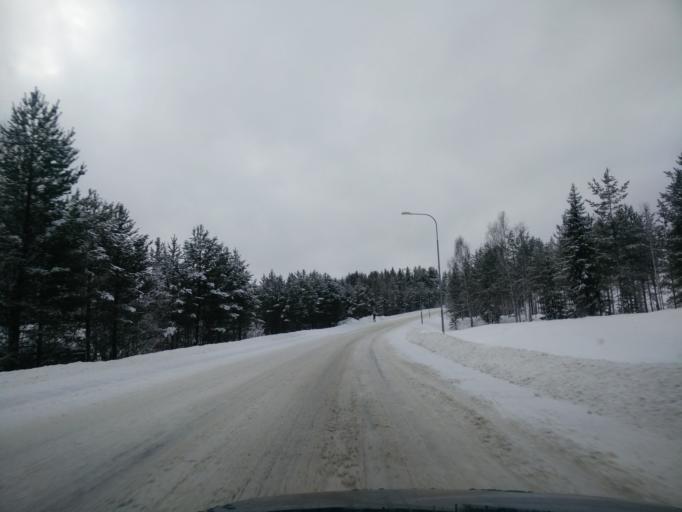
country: SE
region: Vaesternorrland
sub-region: Ange Kommun
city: Ange
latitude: 62.4974
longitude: 15.4829
